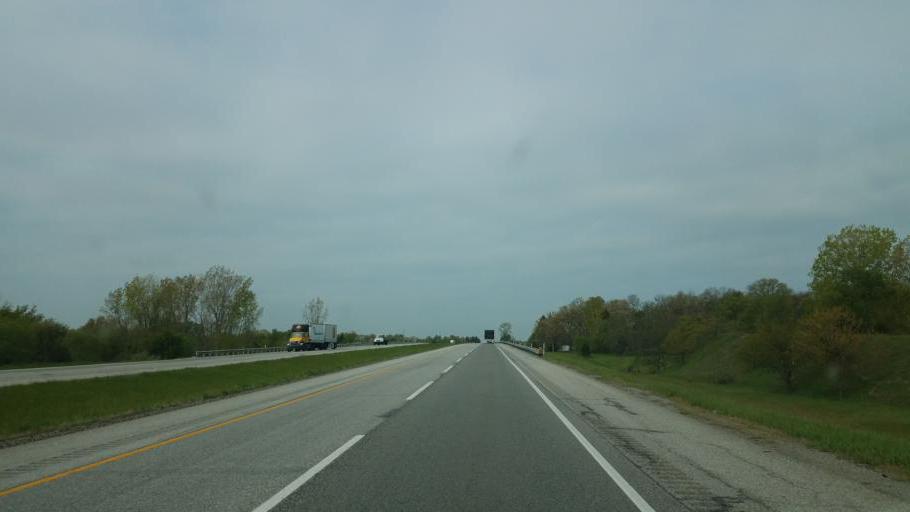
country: US
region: Indiana
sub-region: Elkhart County
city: Bristol
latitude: 41.7342
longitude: -85.8361
